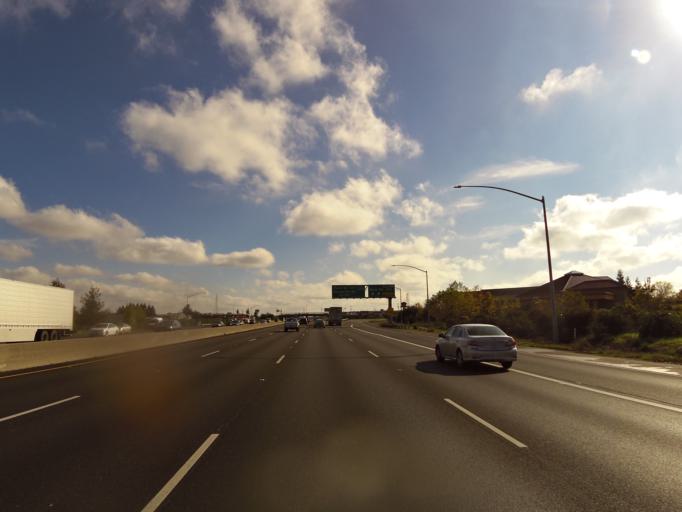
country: US
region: California
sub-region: Sacramento County
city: Florin
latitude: 38.4782
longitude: -121.4272
